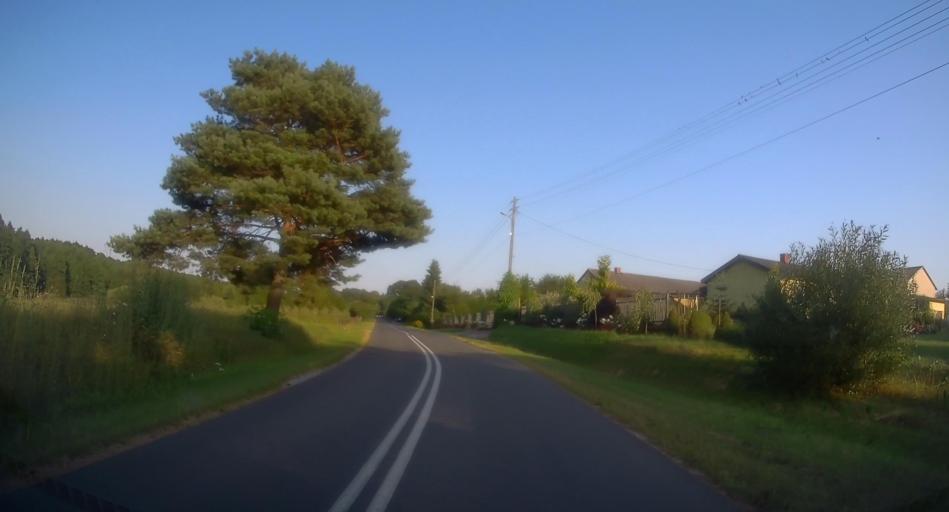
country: PL
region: Lodz Voivodeship
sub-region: Powiat skierniewicki
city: Kowiesy
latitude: 51.8951
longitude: 20.3807
